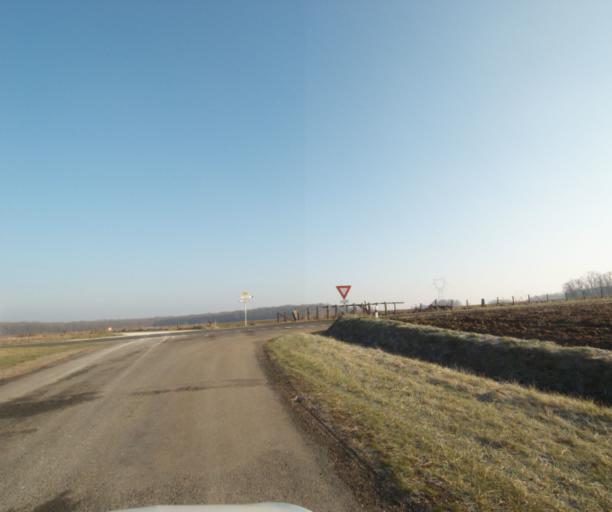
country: FR
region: Champagne-Ardenne
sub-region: Departement de la Haute-Marne
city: Montier-en-Der
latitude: 48.5065
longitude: 4.7316
